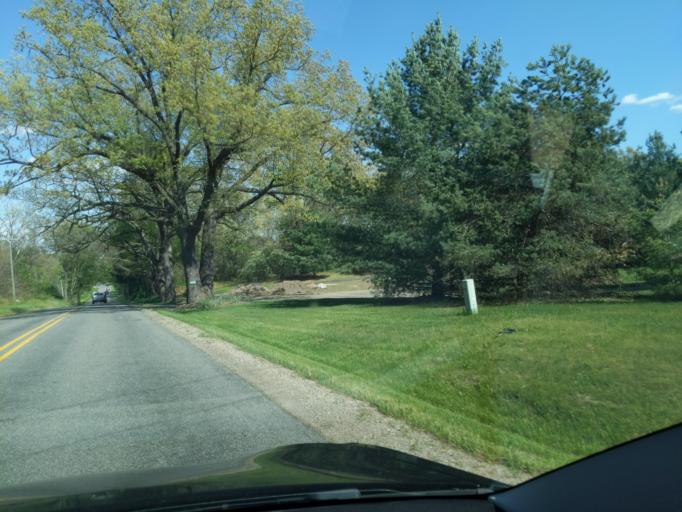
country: US
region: Michigan
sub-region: Kent County
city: Caledonia
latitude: 42.7979
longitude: -85.4538
